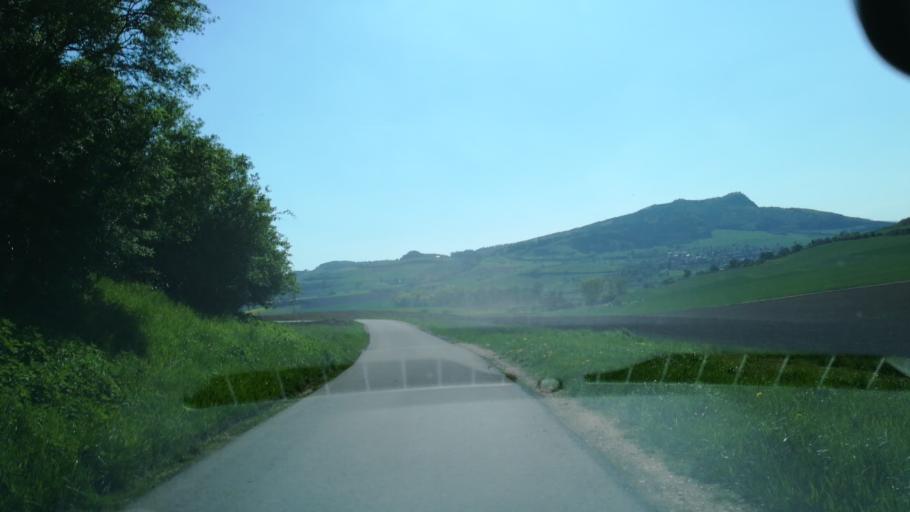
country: DE
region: Baden-Wuerttemberg
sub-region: Freiburg Region
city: Muhlhausen-Ehingen
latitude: 47.8024
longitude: 8.7988
